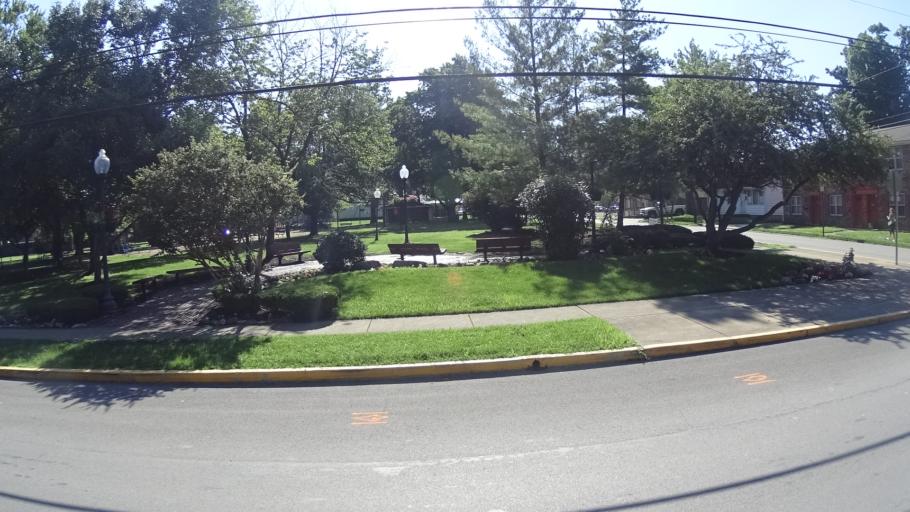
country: US
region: Indiana
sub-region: Madison County
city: Pendleton
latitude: 40.0039
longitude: -85.7457
